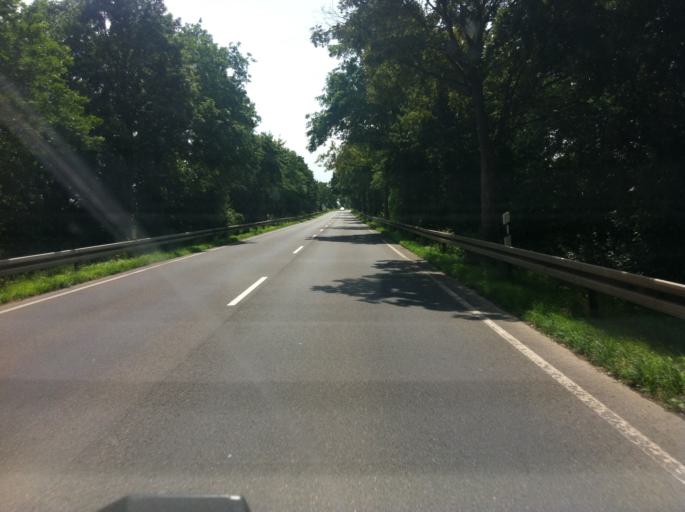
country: DE
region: North Rhine-Westphalia
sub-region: Regierungsbezirk Koln
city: Weilerswist
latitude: 50.7271
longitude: 6.8252
